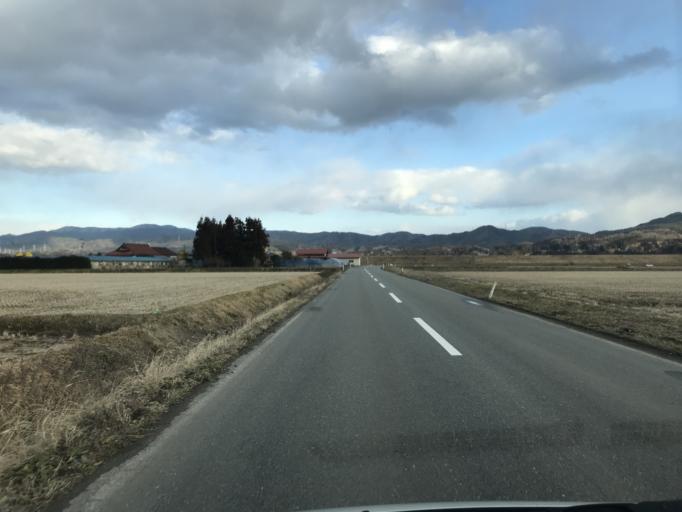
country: JP
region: Iwate
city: Mizusawa
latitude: 39.0575
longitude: 141.1494
